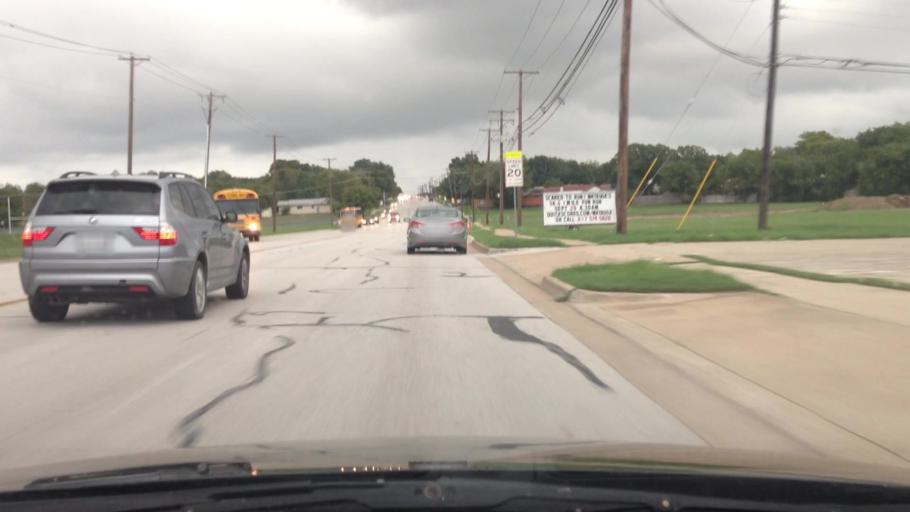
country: US
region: Texas
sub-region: Tarrant County
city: Watauga
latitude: 32.8605
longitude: -97.2495
